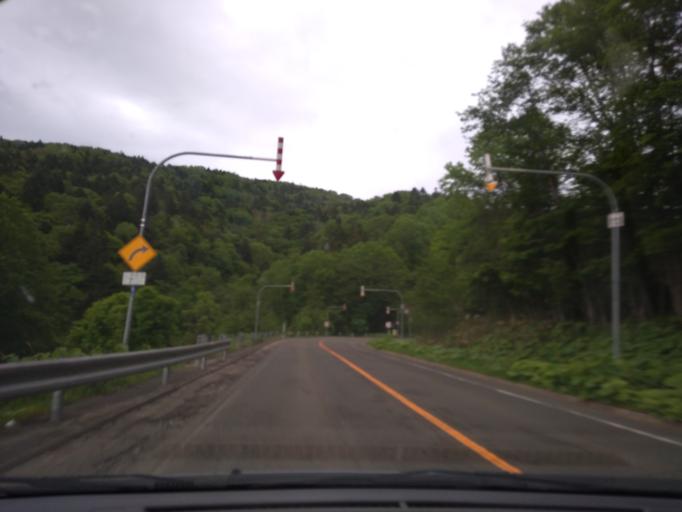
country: JP
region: Hokkaido
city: Shimo-furano
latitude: 43.0928
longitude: 142.4049
